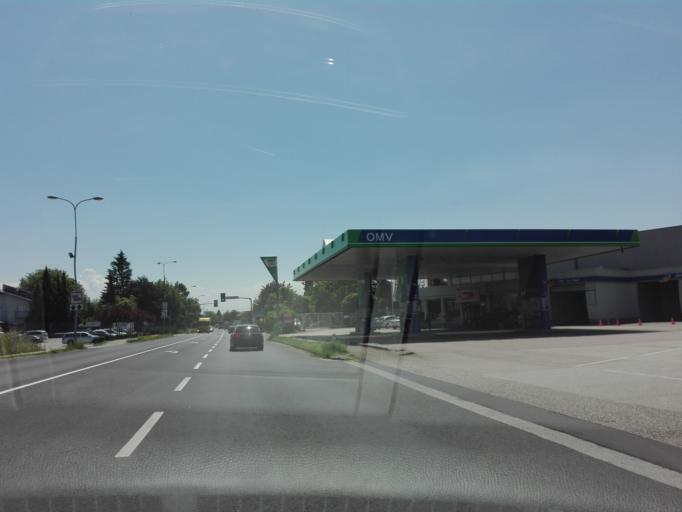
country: AT
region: Upper Austria
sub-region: Politischer Bezirk Linz-Land
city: Traun
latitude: 48.2040
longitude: 14.2472
